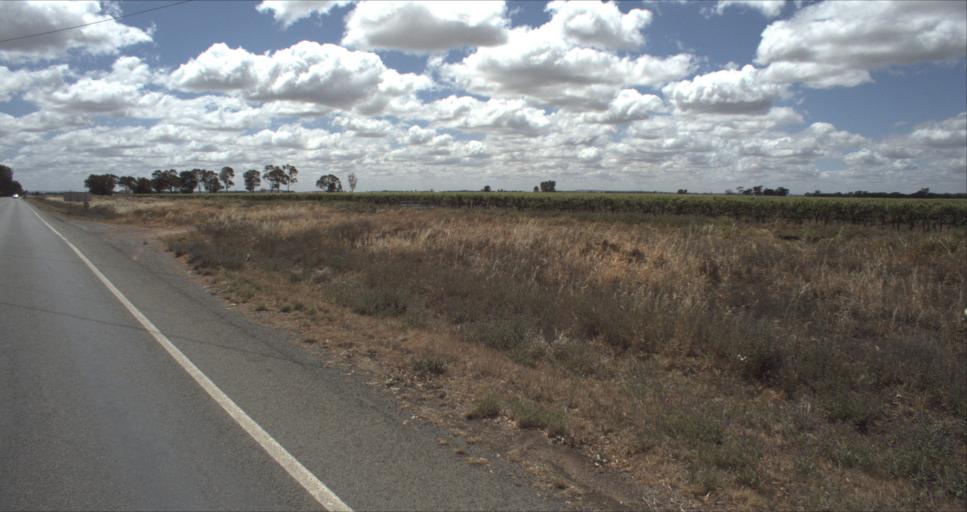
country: AU
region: New South Wales
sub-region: Murrumbidgee Shire
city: Darlington Point
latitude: -34.5067
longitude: 146.1871
